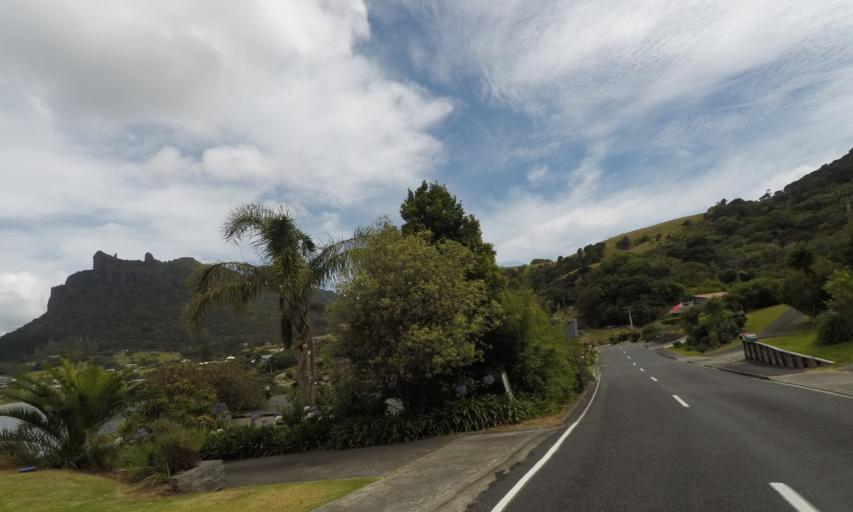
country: NZ
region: Northland
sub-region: Whangarei
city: Ruakaka
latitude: -35.8294
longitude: 174.5301
